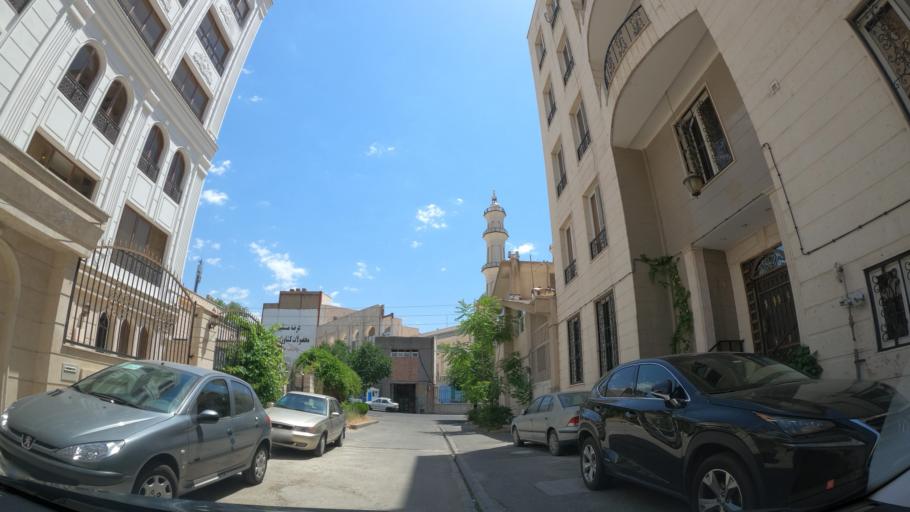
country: IR
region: Tehran
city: Tajrish
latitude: 35.7875
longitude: 51.3879
